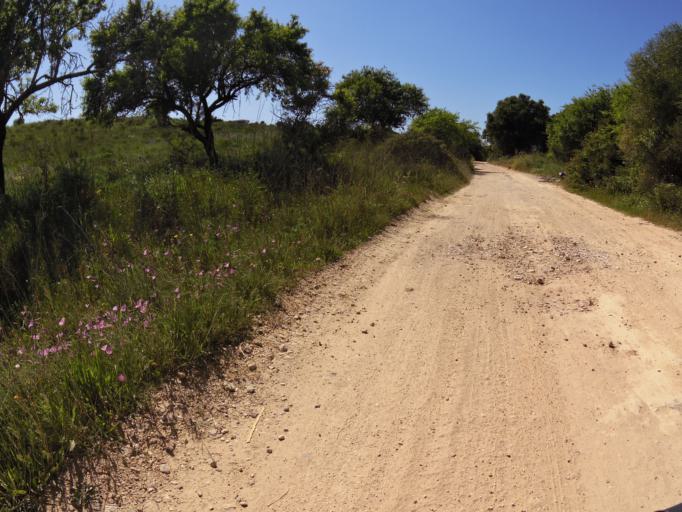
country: PT
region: Faro
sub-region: Lagos
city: Lagos
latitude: 37.0994
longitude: -8.7075
